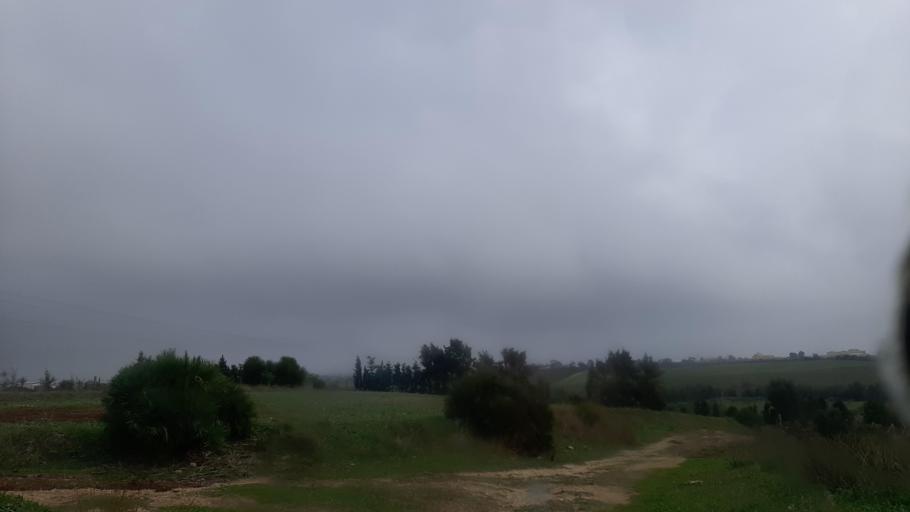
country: TN
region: Nabul
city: Qulaybiyah
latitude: 36.8278
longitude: 11.0353
